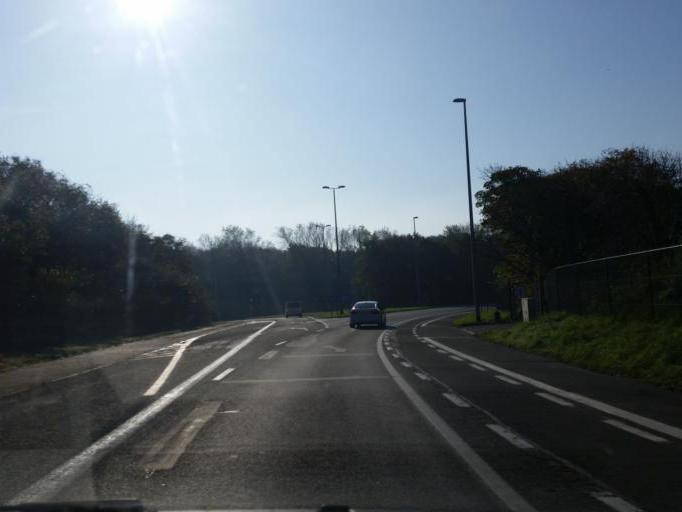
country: BE
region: Flanders
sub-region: Provincie West-Vlaanderen
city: De Haan
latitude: 51.2718
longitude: 3.0220
